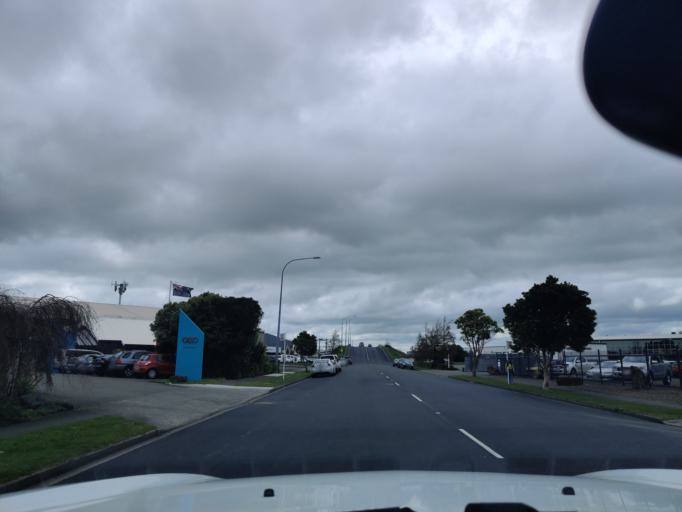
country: NZ
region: Manawatu-Wanganui
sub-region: Palmerston North City
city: Palmerston North
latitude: -40.3395
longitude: 175.6433
